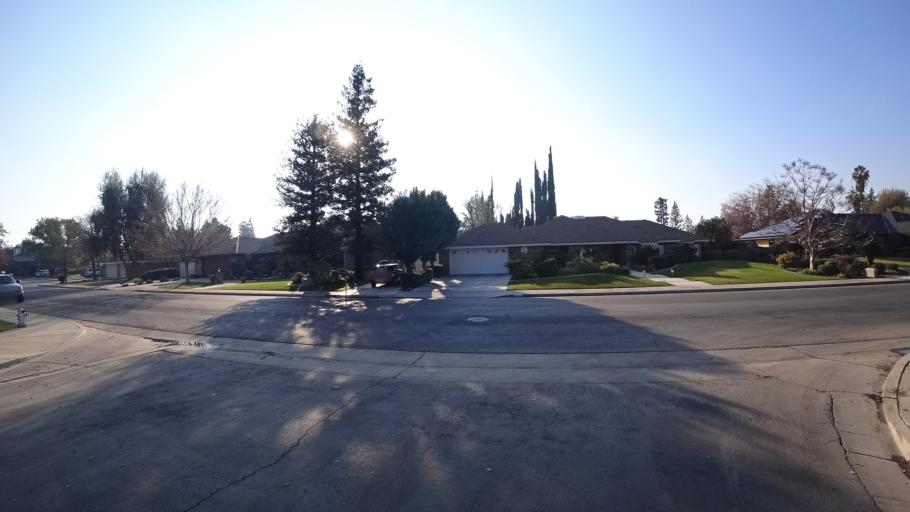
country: US
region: California
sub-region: Kern County
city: Greenacres
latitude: 35.3351
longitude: -119.0977
